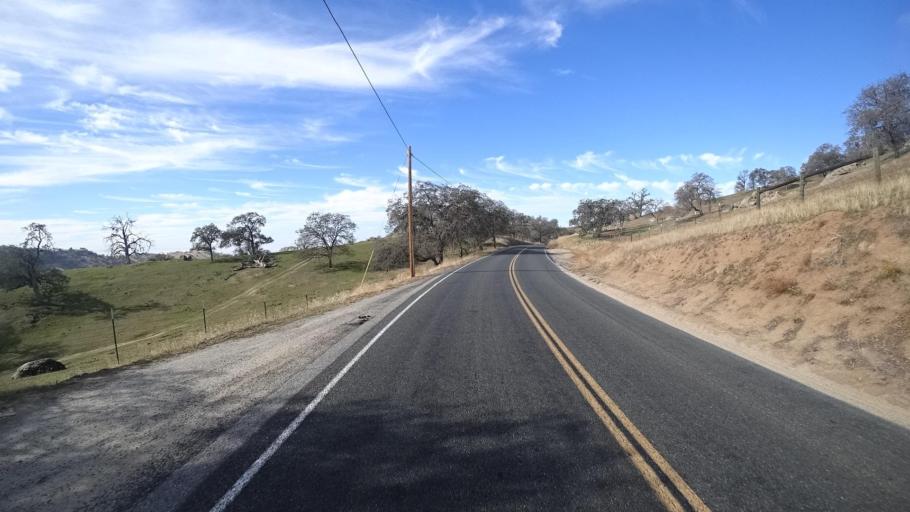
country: US
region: California
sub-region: Kern County
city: Alta Sierra
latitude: 35.6266
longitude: -118.8083
